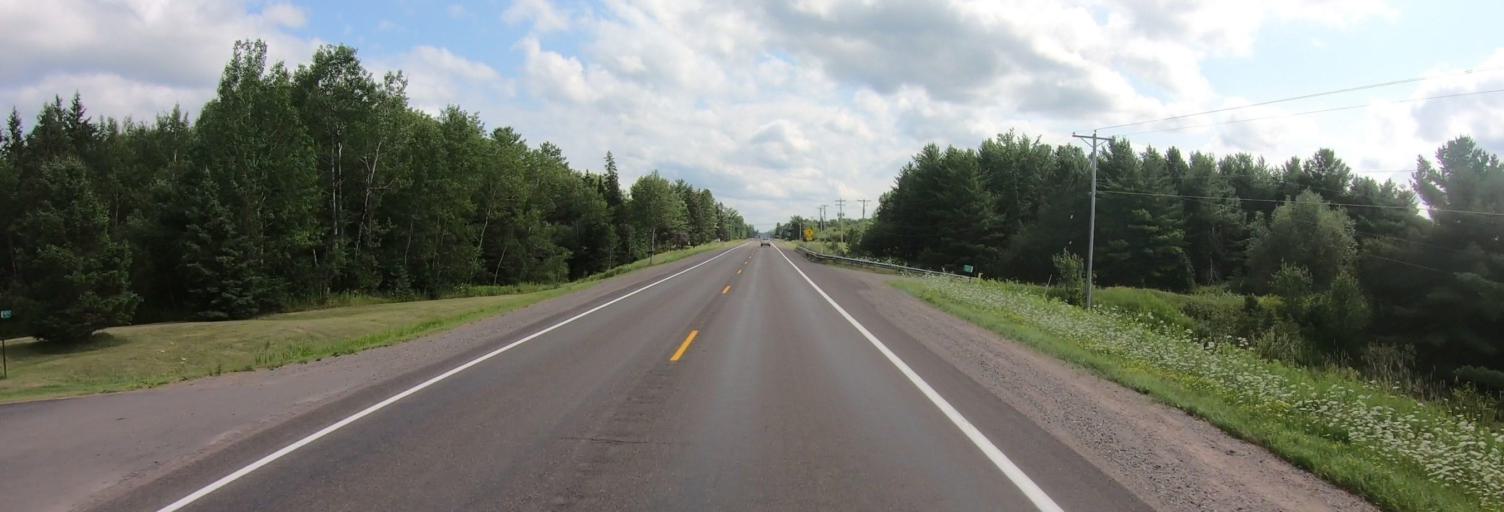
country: US
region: Michigan
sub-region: Ontonagon County
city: Ontonagon
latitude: 46.5474
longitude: -89.1787
